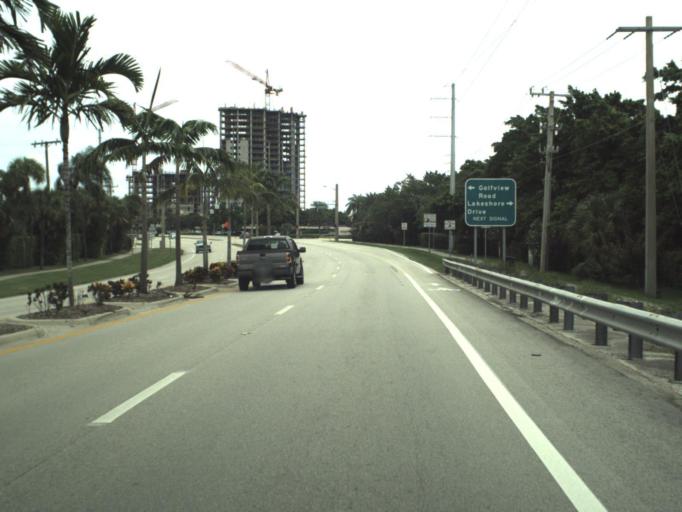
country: US
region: Florida
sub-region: Palm Beach County
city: North Palm Beach
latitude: 26.8327
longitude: -80.0599
